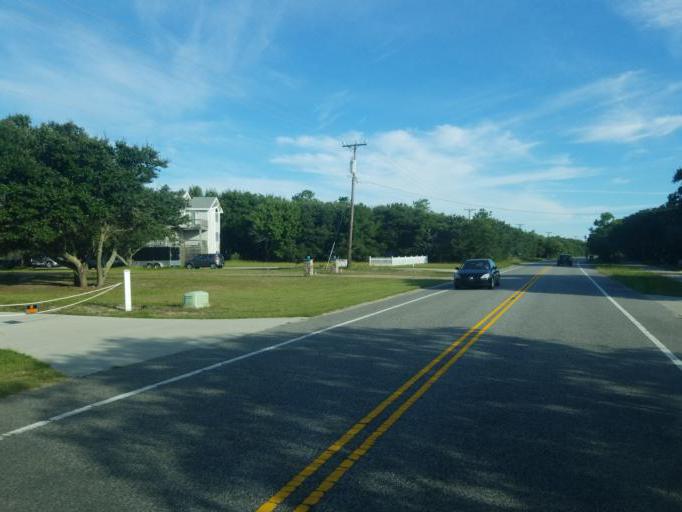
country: US
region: North Carolina
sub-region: Dare County
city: Southern Shores
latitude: 36.2924
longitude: -75.8020
